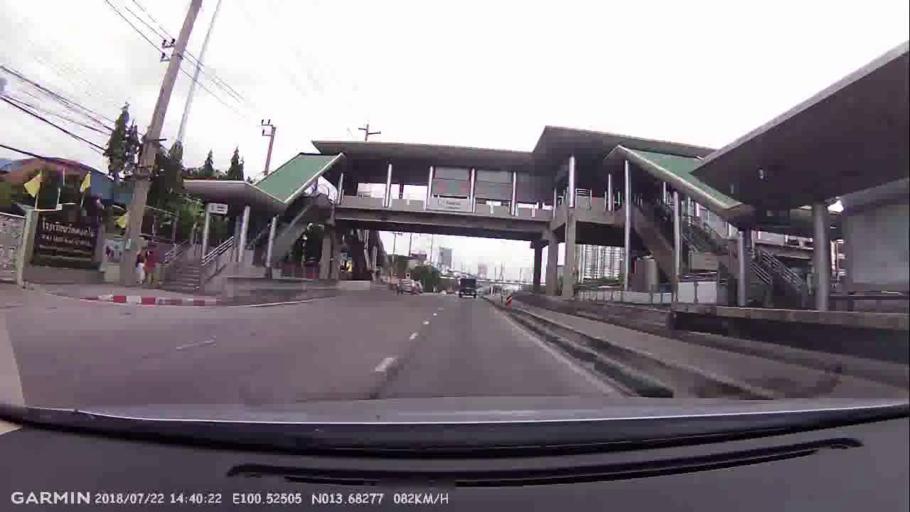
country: TH
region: Bangkok
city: Rat Burana
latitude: 13.6827
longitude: 100.5252
